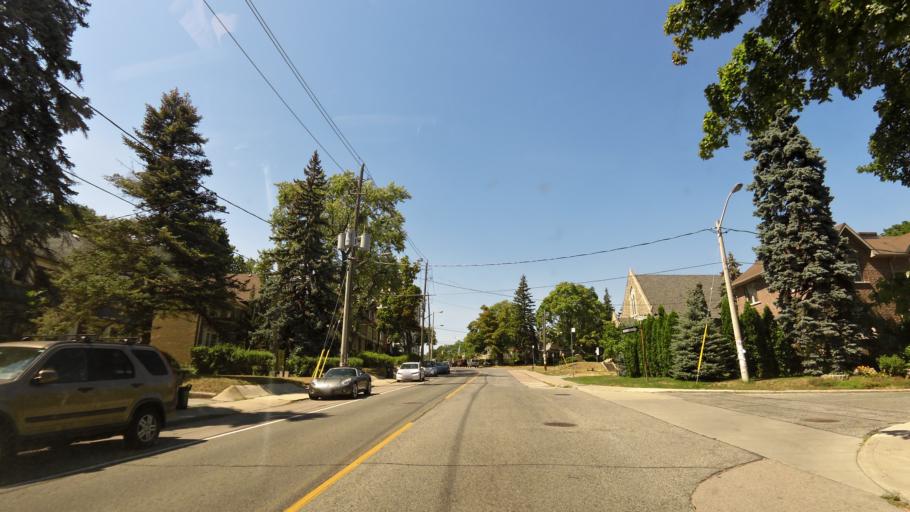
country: CA
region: Ontario
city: Etobicoke
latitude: 43.6471
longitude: -79.4844
